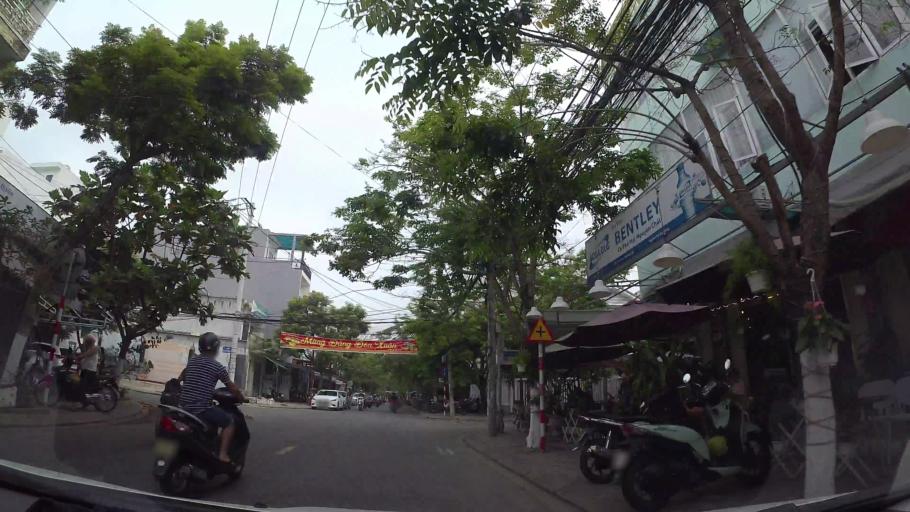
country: VN
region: Da Nang
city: Son Tra
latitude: 16.0512
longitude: 108.2403
